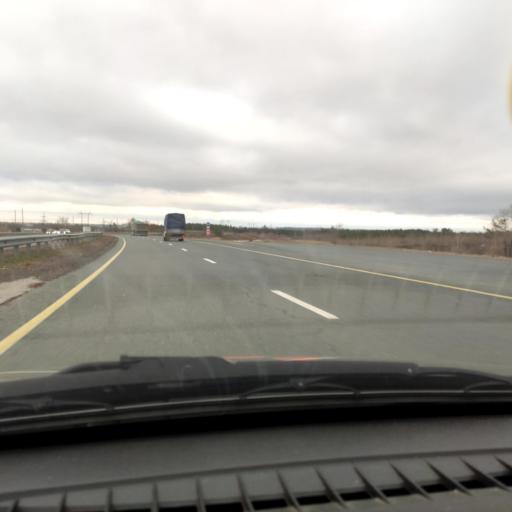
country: RU
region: Samara
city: Zhigulevsk
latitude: 53.5139
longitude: 49.5375
